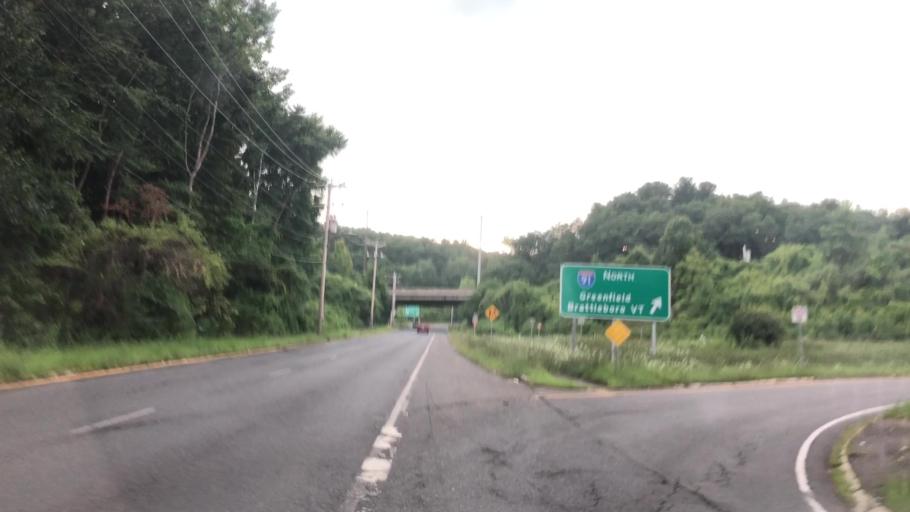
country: US
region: Massachusetts
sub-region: Hampden County
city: Holyoke
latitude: 42.2130
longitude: -72.6305
